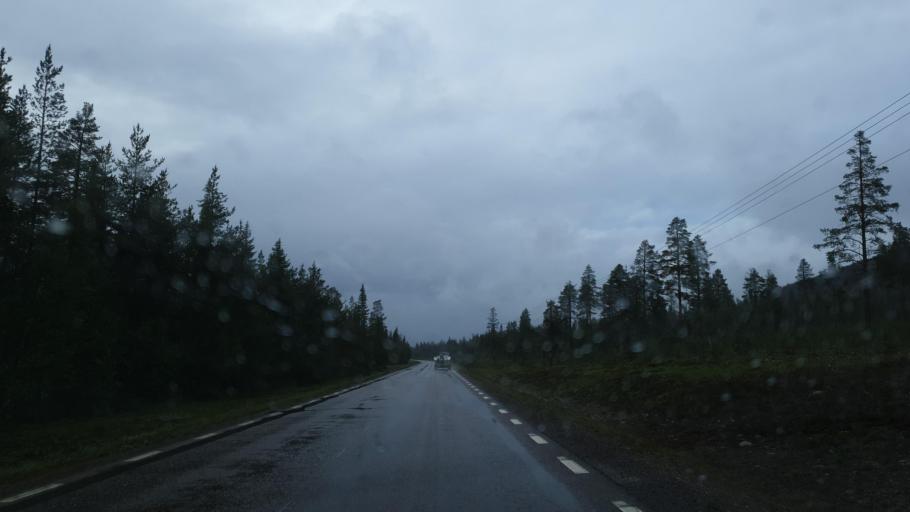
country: SE
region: Norrbotten
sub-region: Arvidsjaurs Kommun
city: Arvidsjaur
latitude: 65.6977
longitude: 18.7665
